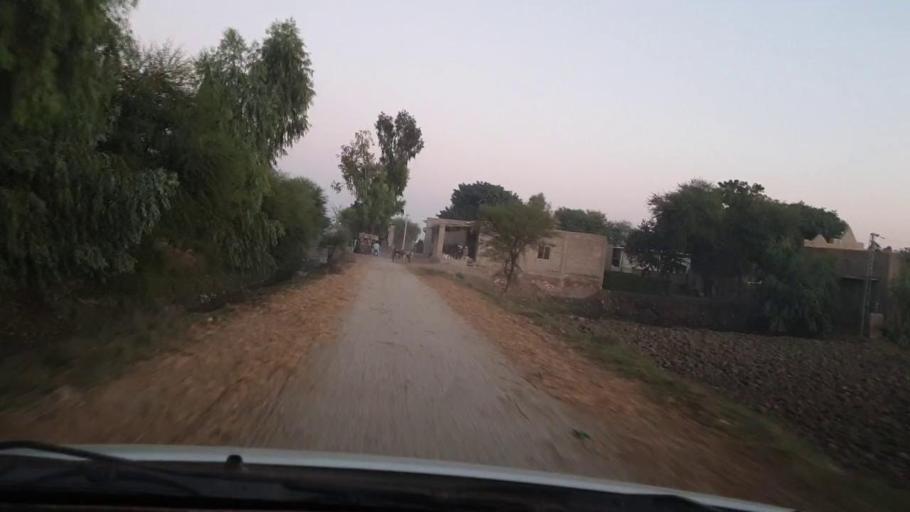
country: PK
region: Sindh
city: Khairpur Nathan Shah
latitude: 27.1456
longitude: 67.7055
